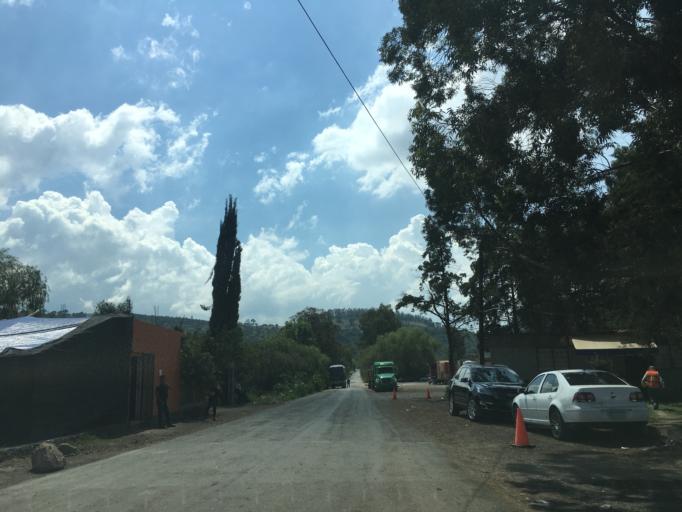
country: MX
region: Michoacan
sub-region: Morelia
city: La Mintzita (Piedra Dura)
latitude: 19.6491
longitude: -101.2646
